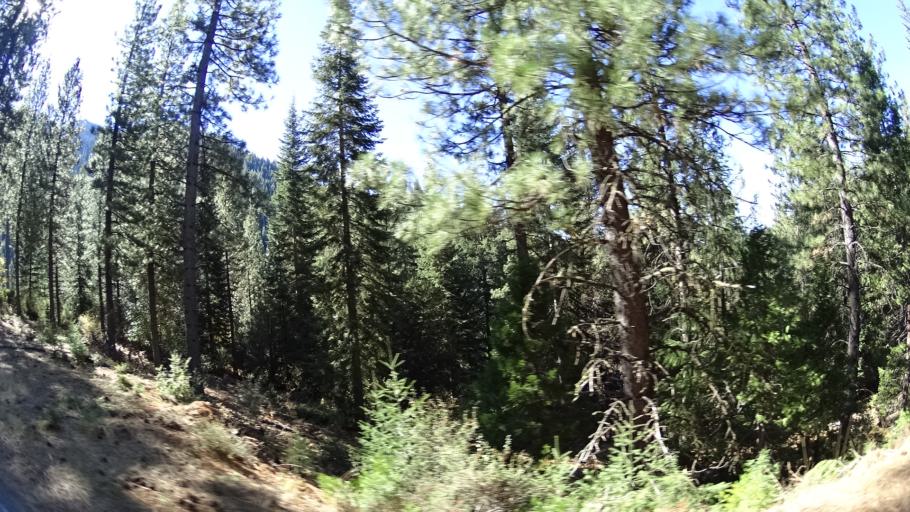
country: US
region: California
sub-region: Trinity County
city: Weaverville
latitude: 41.2258
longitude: -122.9989
